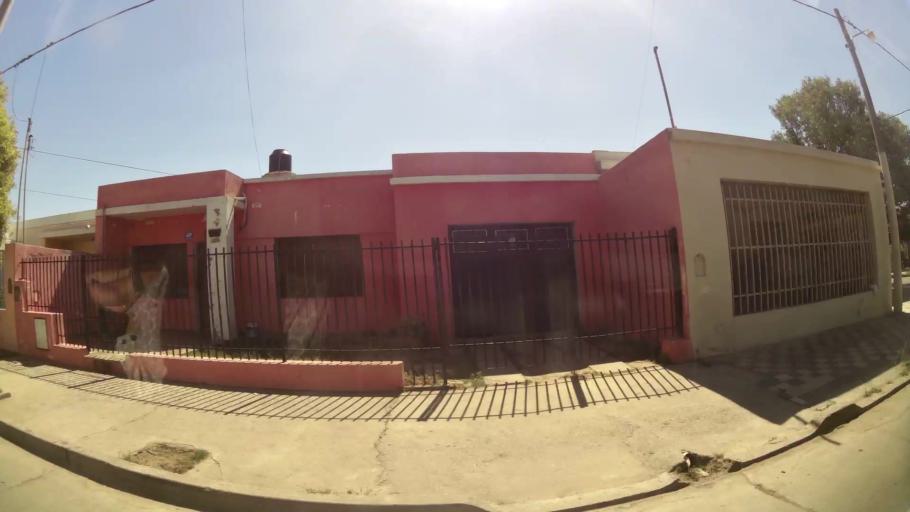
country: AR
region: Cordoba
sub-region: Departamento de Capital
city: Cordoba
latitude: -31.3725
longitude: -64.1366
